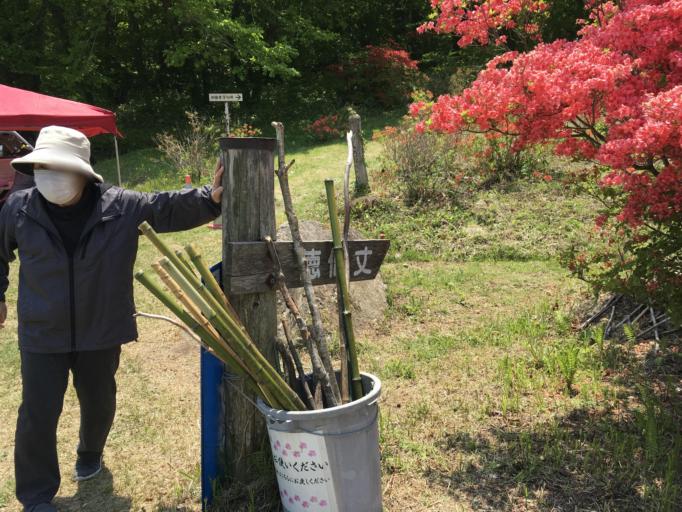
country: JP
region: Iwate
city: Ofunato
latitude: 38.8559
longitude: 141.4701
